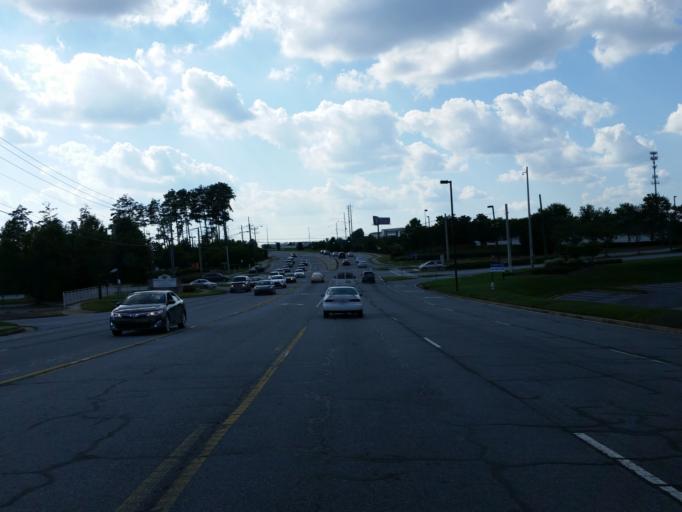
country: US
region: Georgia
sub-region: Gwinnett County
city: Duluth
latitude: 33.9574
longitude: -84.1094
